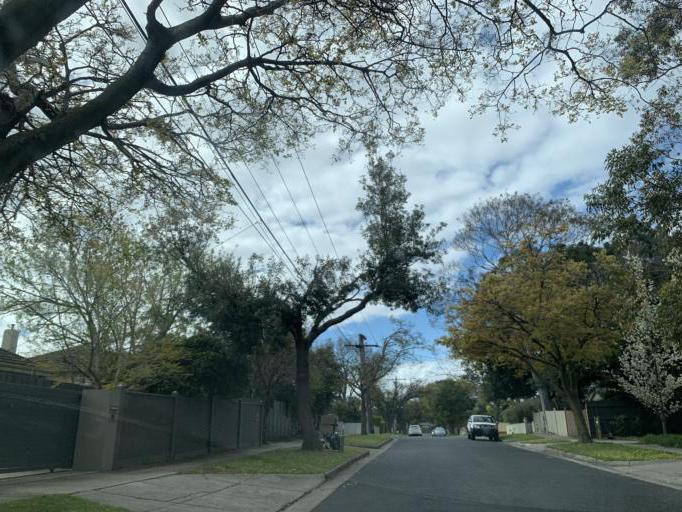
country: AU
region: Victoria
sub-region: Bayside
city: Cheltenham
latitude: -37.9757
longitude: 145.0490
